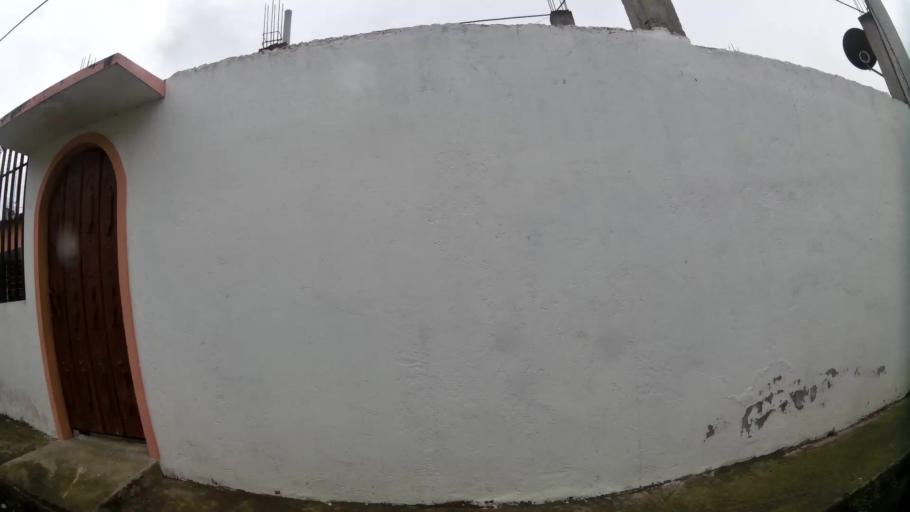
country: EC
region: Pichincha
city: Sangolqui
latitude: -0.2745
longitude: -78.4733
